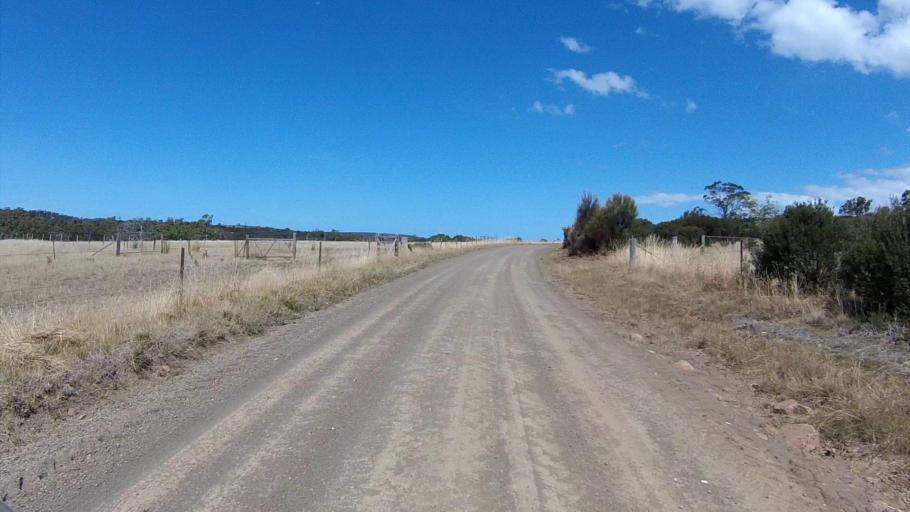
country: AU
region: Tasmania
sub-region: Break O'Day
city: St Helens
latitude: -41.9676
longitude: 148.0742
